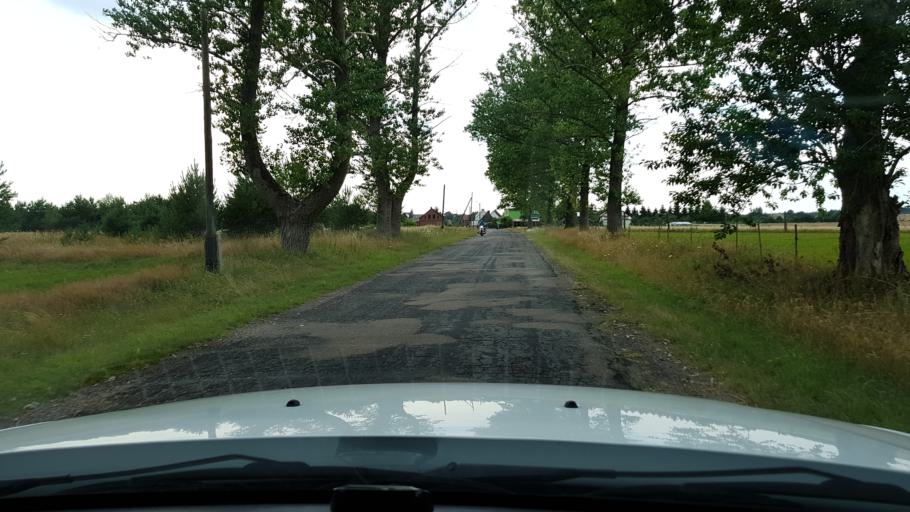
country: PL
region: West Pomeranian Voivodeship
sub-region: Powiat drawski
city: Czaplinek
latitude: 53.4382
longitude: 16.2799
